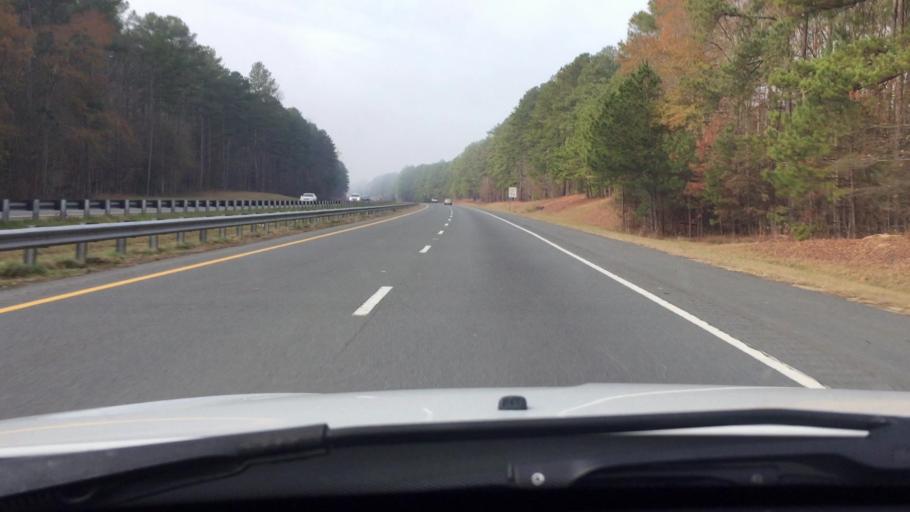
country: US
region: North Carolina
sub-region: Chatham County
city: Fearrington Village
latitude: 35.6442
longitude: -79.0185
